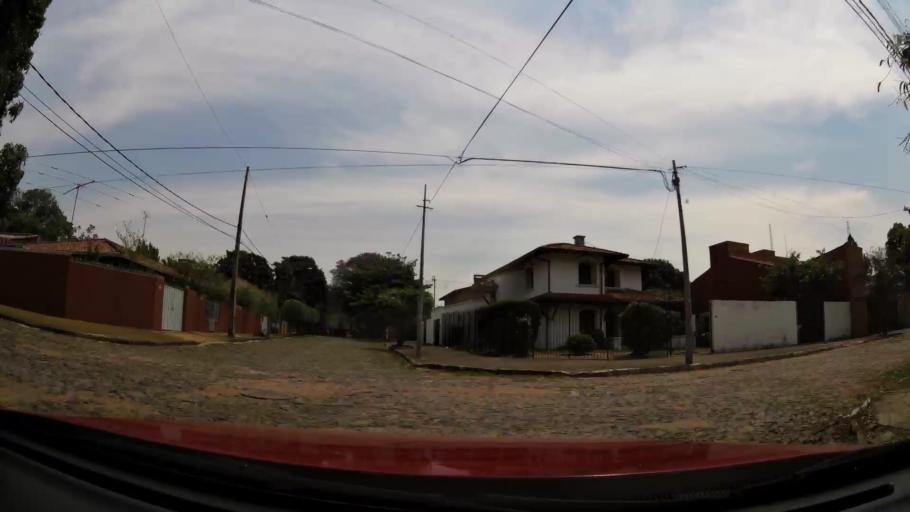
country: PY
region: Asuncion
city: Asuncion
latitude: -25.2710
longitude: -57.5950
